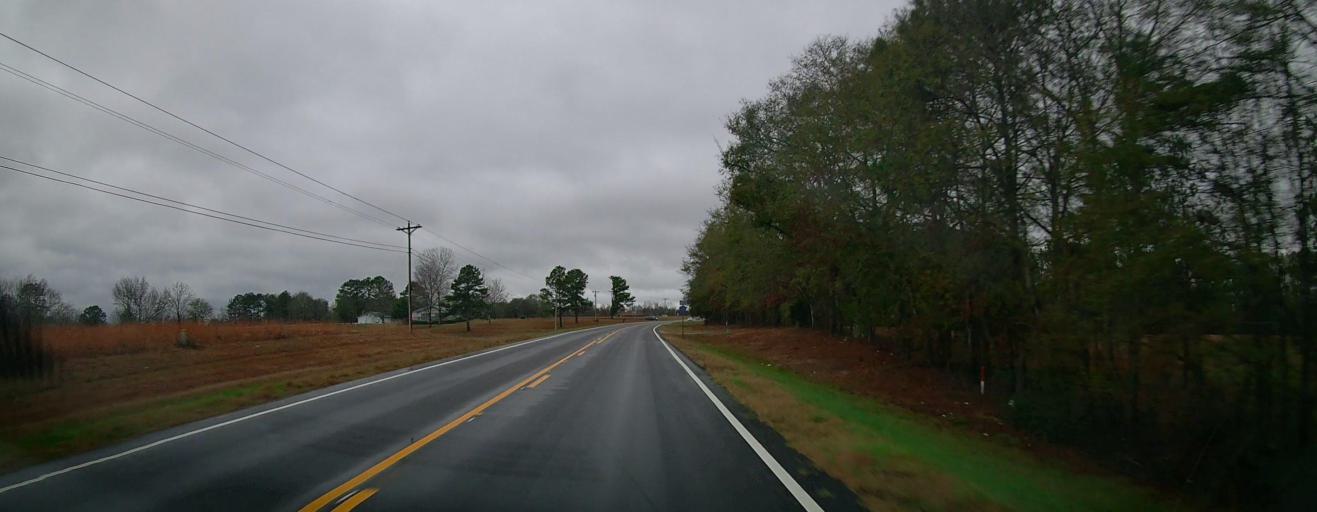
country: US
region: Alabama
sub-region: Chilton County
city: Thorsby
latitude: 32.7843
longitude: -86.8988
